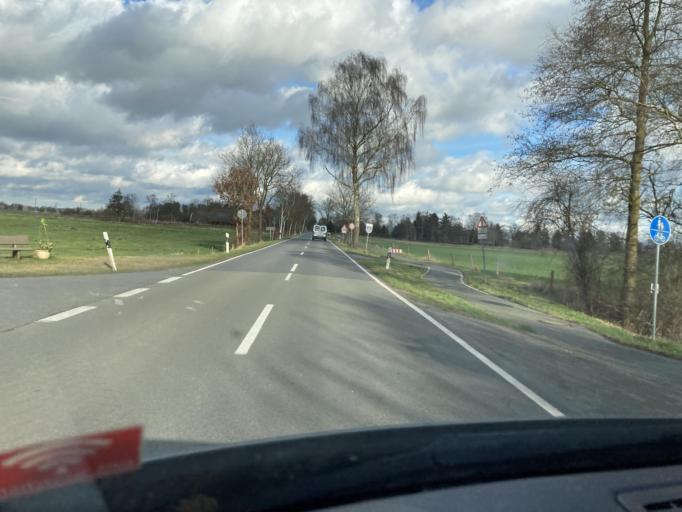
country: DE
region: Lower Saxony
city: Friedeburg
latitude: 53.3732
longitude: 7.8226
